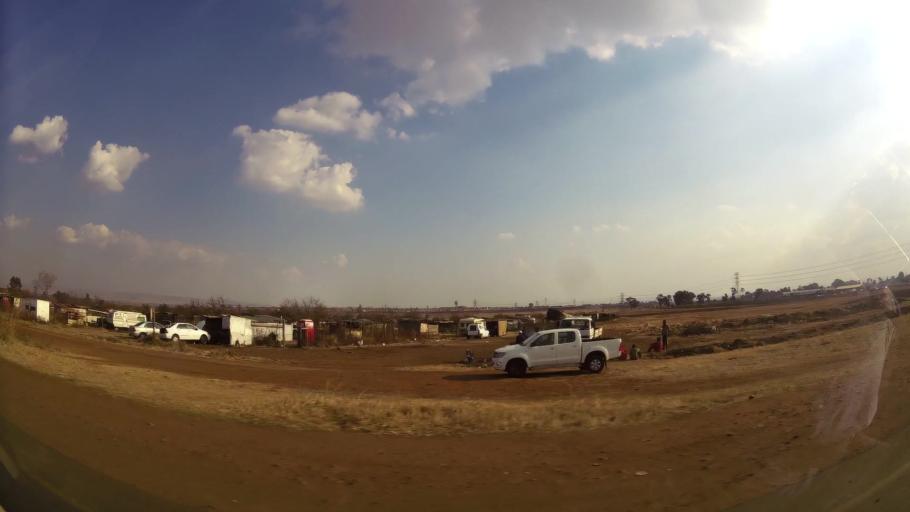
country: ZA
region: Gauteng
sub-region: Ekurhuleni Metropolitan Municipality
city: Germiston
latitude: -26.3361
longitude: 28.2337
